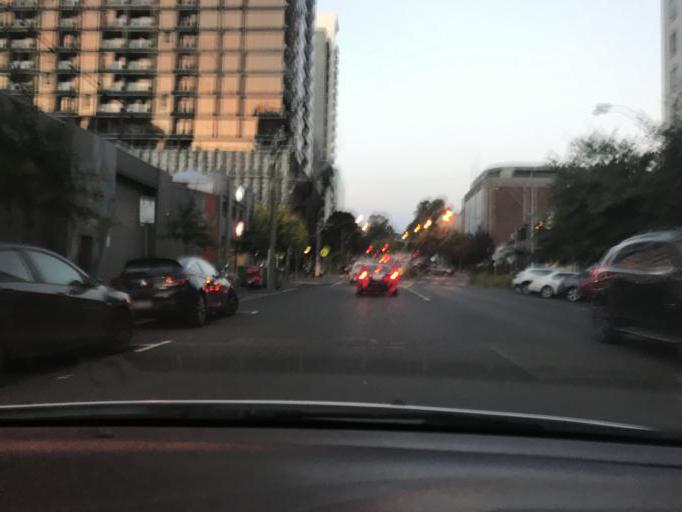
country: AU
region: Victoria
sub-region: Port Phillip
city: South Melbourne
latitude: -37.8307
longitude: 144.9685
